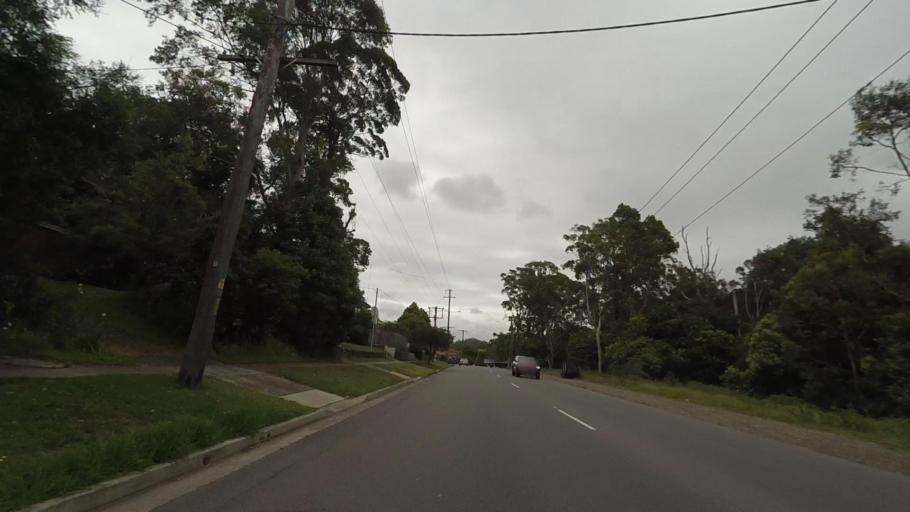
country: AU
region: New South Wales
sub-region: Lake Macquarie Shire
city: Kotara
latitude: -32.9430
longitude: 151.6962
